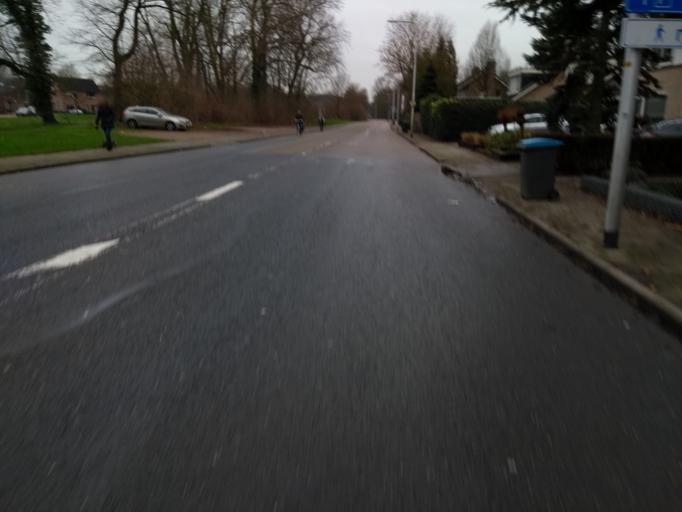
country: NL
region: Overijssel
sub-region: Gemeente Almelo
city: Almelo
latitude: 52.3524
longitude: 6.6488
